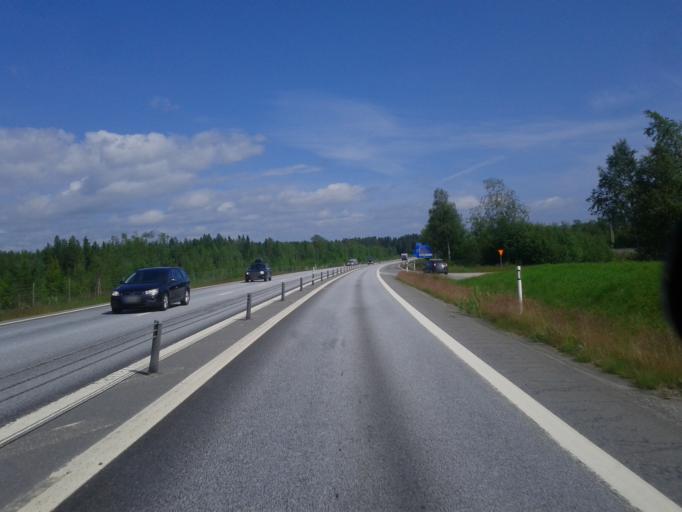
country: SE
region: Vaesterbotten
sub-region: Nordmalings Kommun
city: Nordmaling
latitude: 63.5727
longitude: 19.4421
